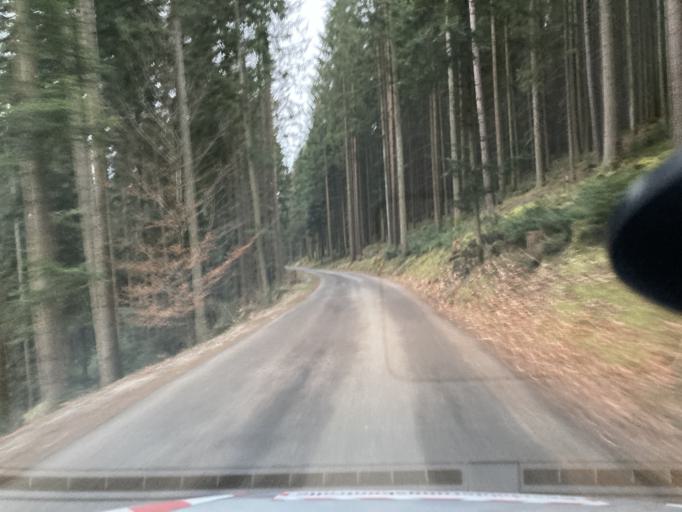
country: DE
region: Baden-Wuerttemberg
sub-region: Karlsruhe Region
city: Neubulach
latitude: 48.6691
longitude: 8.6498
